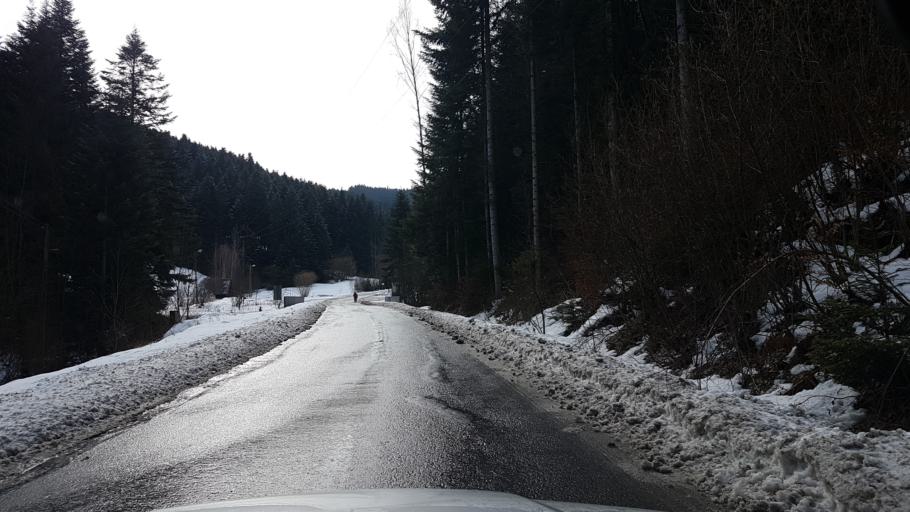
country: PL
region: Lesser Poland Voivodeship
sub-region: Powiat nowosadecki
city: Piwniczna-Zdroj
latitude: 49.4223
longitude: 20.6498
